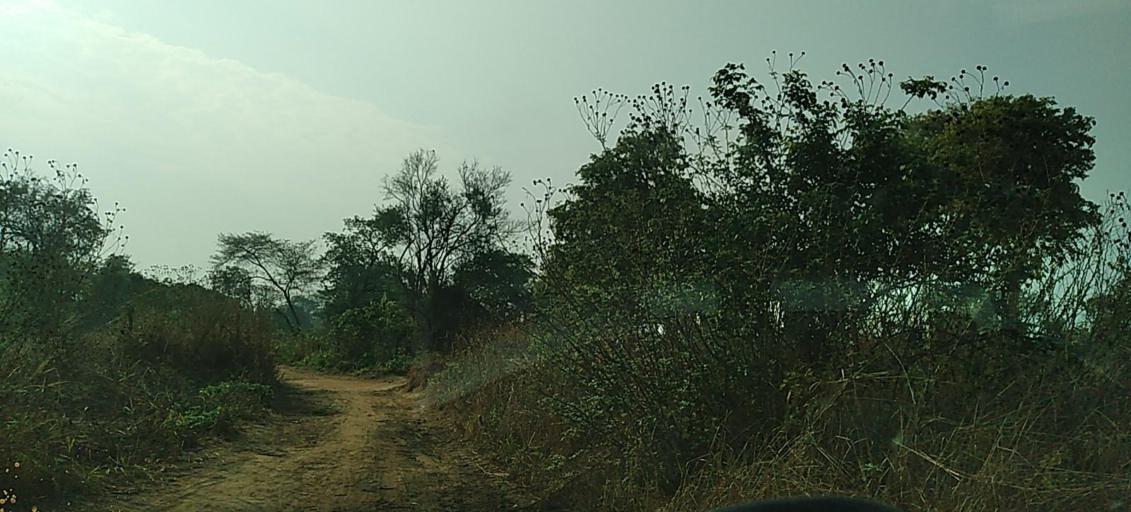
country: ZM
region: North-Western
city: Solwezi
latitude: -12.3556
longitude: 26.5452
